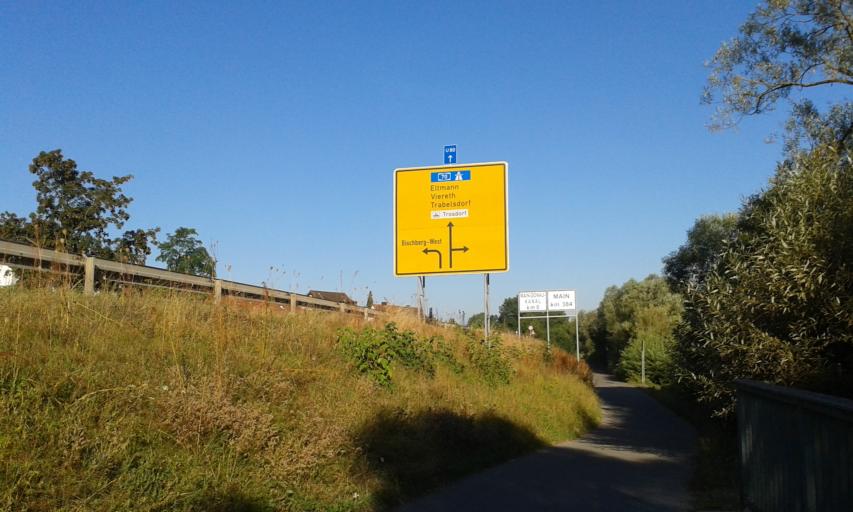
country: DE
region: Bavaria
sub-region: Upper Franconia
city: Bischberg
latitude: 49.9142
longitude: 10.8279
